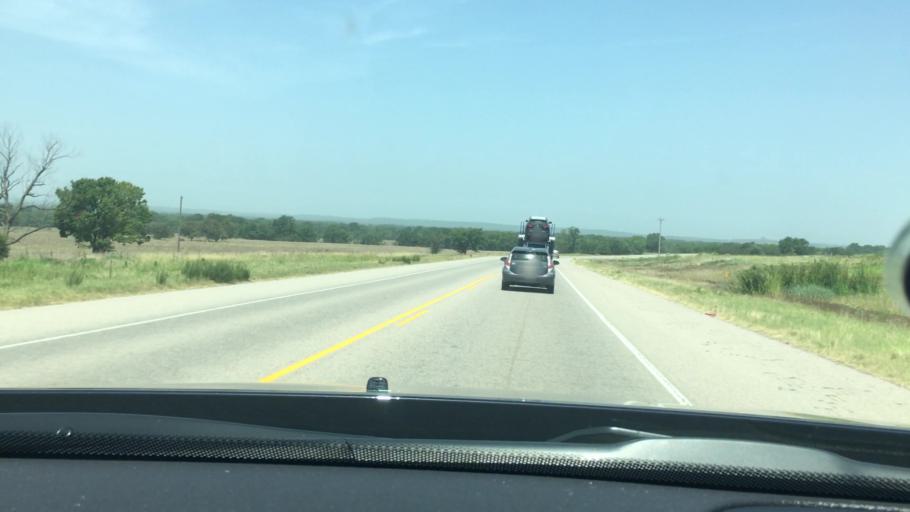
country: US
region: Oklahoma
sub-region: Pontotoc County
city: Ada
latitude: 34.6825
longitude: -96.5868
